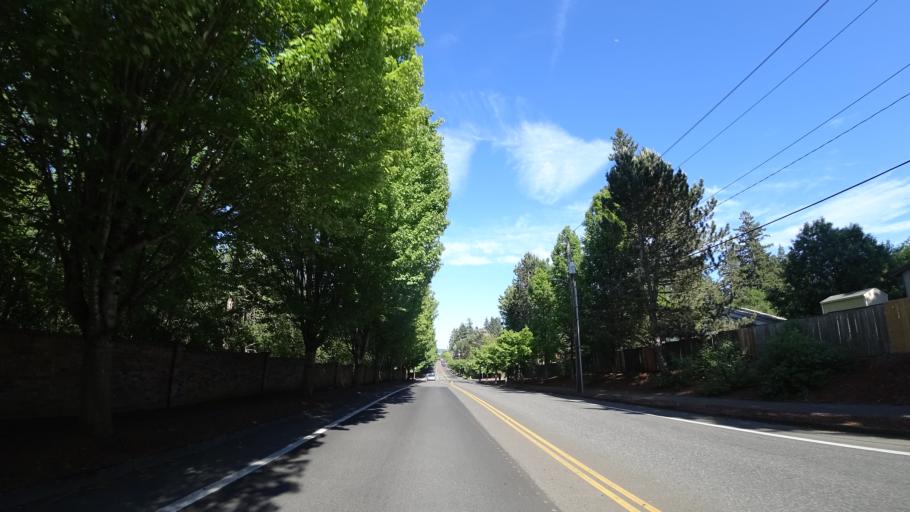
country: US
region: Oregon
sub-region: Washington County
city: Beaverton
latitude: 45.4548
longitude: -122.8116
